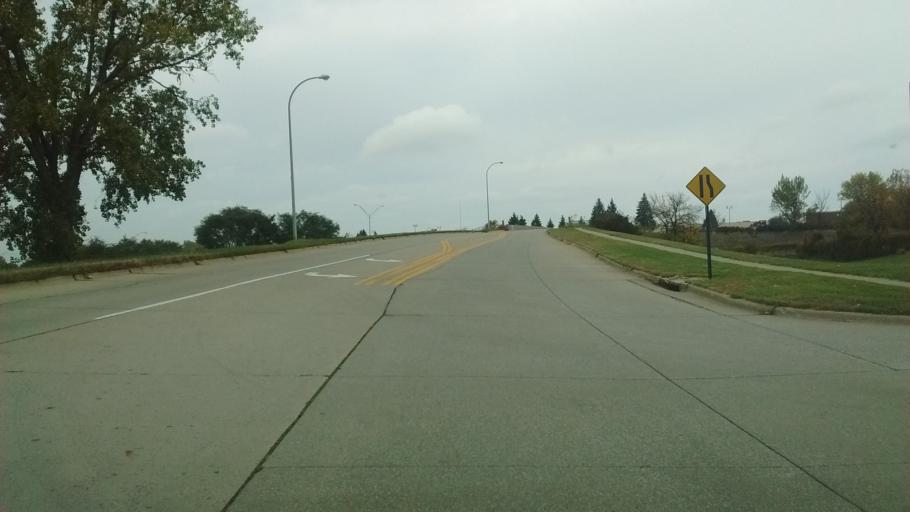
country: US
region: Iowa
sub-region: Woodbury County
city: Sergeant Bluff
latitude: 42.4421
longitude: -96.3523
